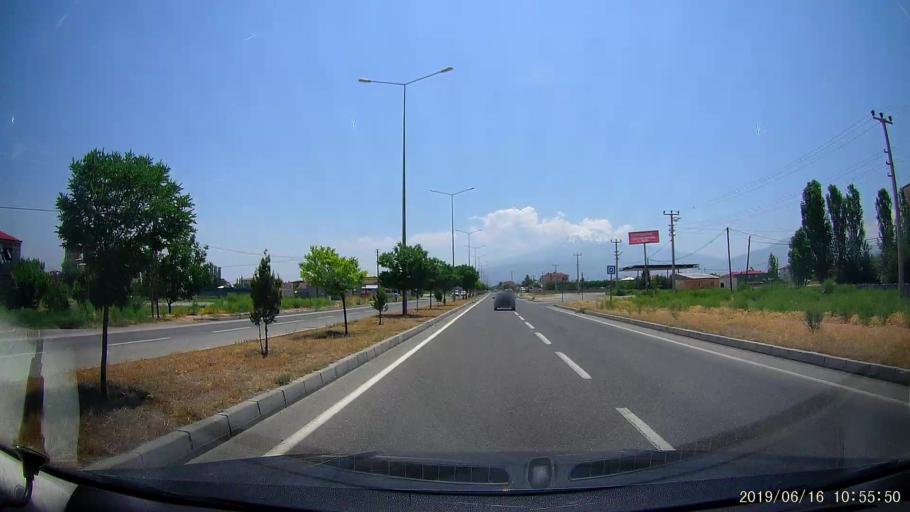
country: TR
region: Igdir
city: Igdir
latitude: 39.9340
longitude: 44.0148
